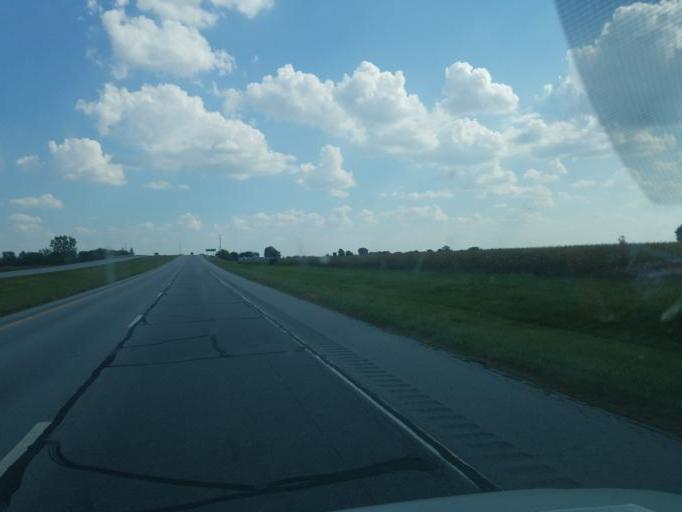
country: US
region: Ohio
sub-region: Allen County
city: Delphos
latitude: 40.8696
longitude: -84.3359
